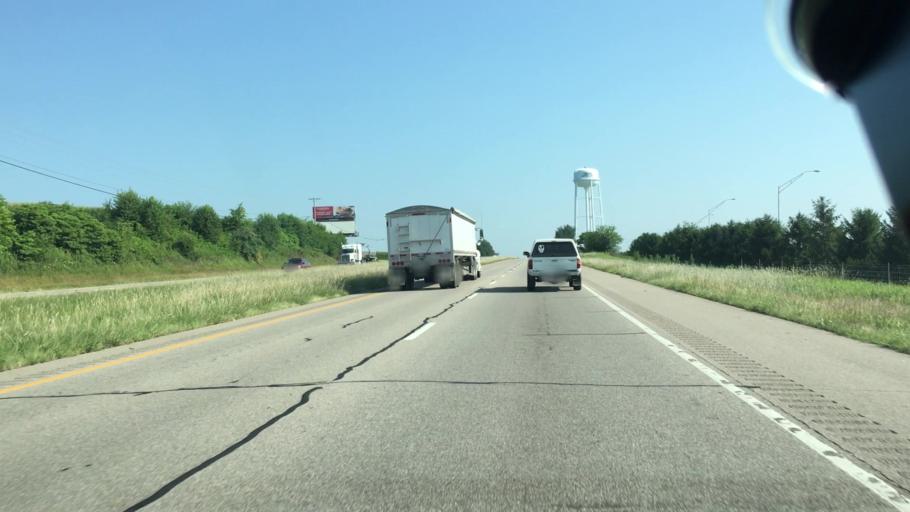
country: US
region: Indiana
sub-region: Gibson County
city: Fort Branch
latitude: 38.2860
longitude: -87.5675
